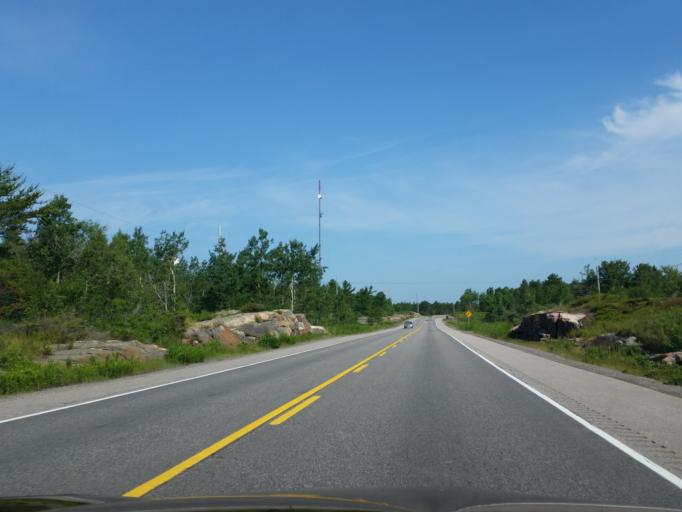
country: CA
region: Ontario
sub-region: Parry Sound District
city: Parry Sound
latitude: 45.7913
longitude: -80.5294
